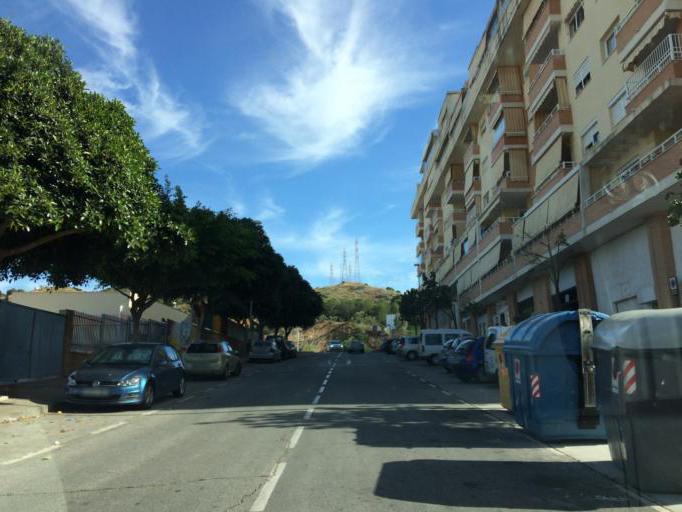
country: ES
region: Andalusia
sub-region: Provincia de Malaga
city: Malaga
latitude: 36.7256
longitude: -4.4799
